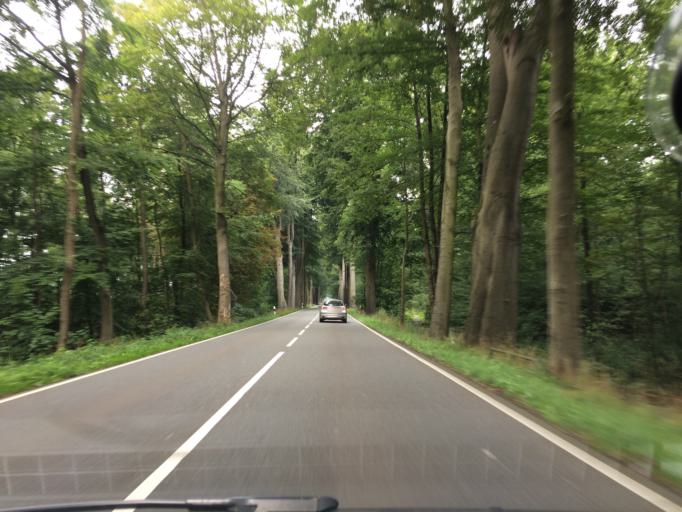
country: DE
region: North Rhine-Westphalia
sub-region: Regierungsbezirk Munster
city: Klein Reken
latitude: 51.7365
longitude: 7.0052
